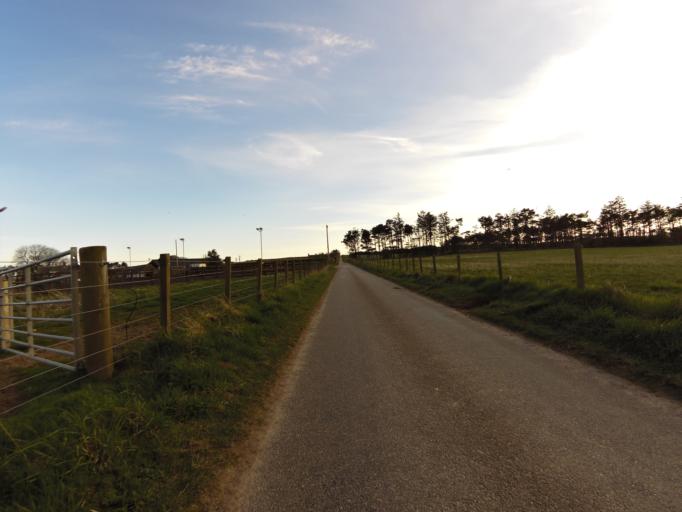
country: GB
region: Scotland
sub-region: Aberdeenshire
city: Stonehaven
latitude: 56.9443
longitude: -2.2201
